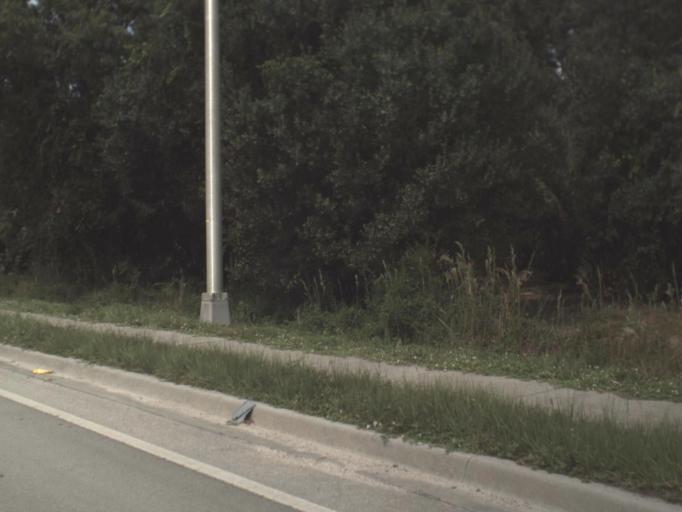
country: US
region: Florida
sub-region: Okeechobee County
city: Okeechobee
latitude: 27.2436
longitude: -80.8514
